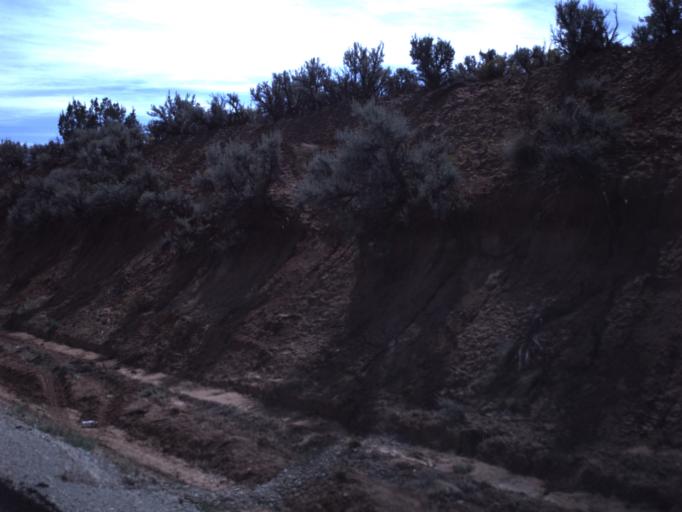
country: US
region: Utah
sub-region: San Juan County
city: Blanding
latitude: 37.5588
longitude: -109.5758
